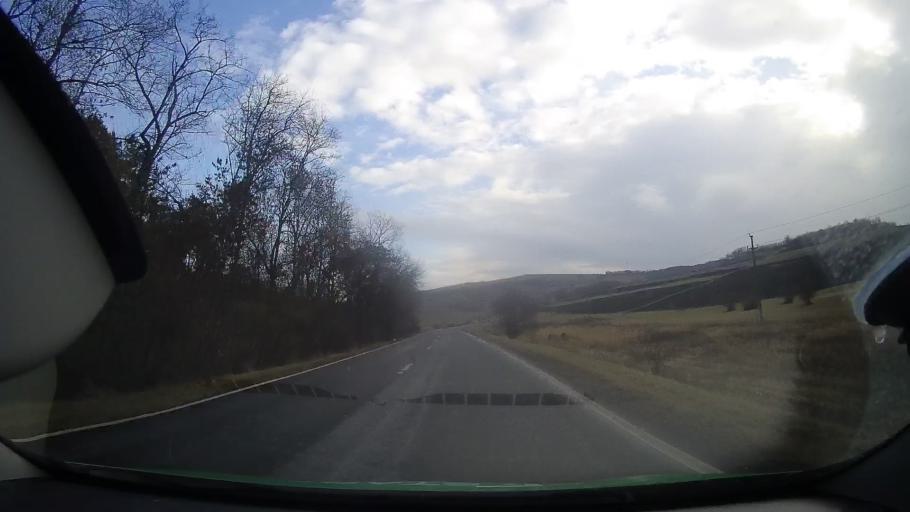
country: RO
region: Mures
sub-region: Comuna Cucerdea
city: Cucerdea
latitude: 46.3645
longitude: 24.2681
